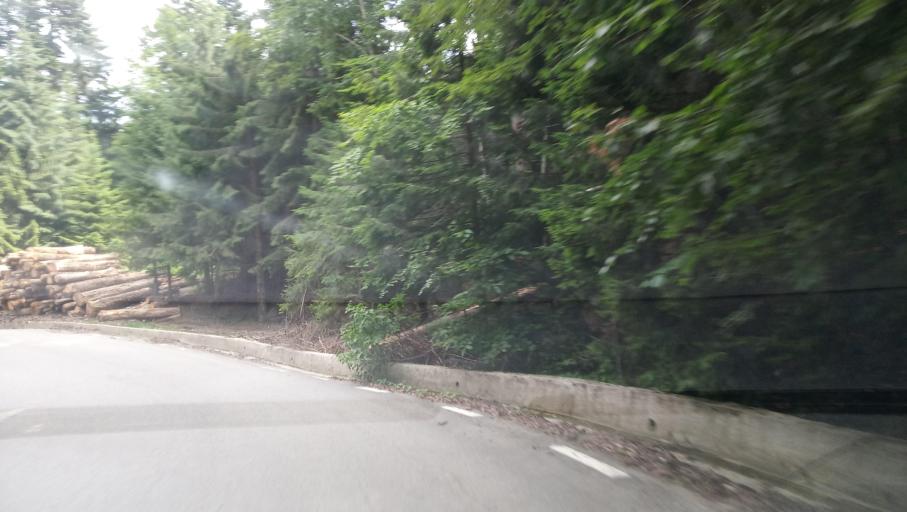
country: RO
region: Prahova
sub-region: Oras Sinaia
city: Sinaia
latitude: 45.3233
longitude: 25.5082
